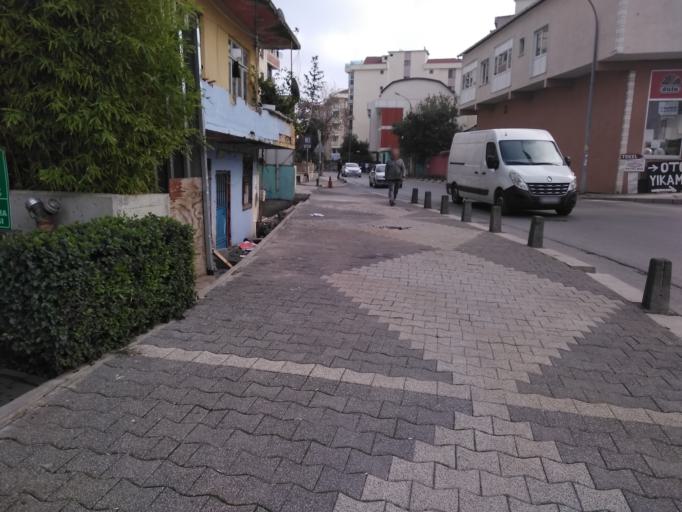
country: TR
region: Istanbul
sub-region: Atasehir
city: Atasehir
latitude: 40.9822
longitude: 29.1102
